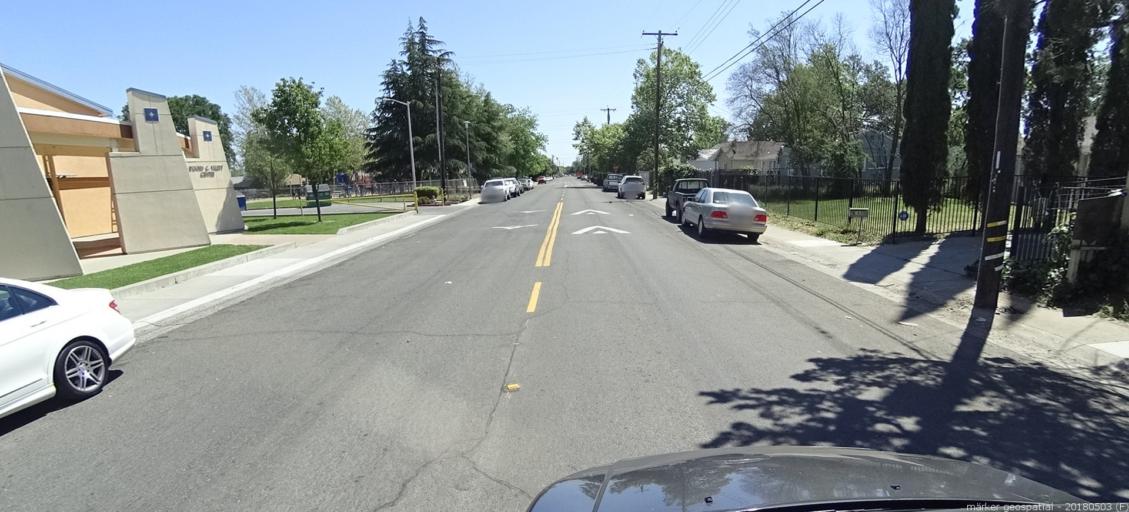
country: US
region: California
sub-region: Sacramento County
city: Arden-Arcade
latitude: 38.6328
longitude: -121.4245
